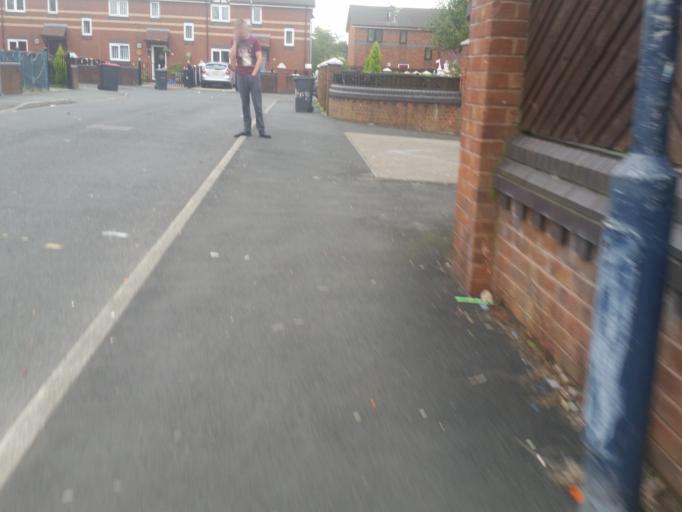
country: GB
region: England
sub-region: City and Borough of Salford
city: Salford
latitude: 53.4767
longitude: -2.2814
